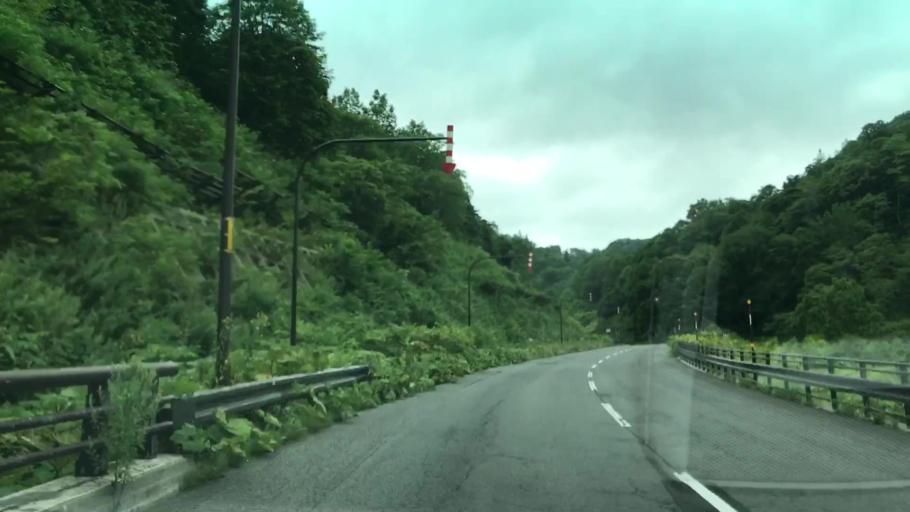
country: JP
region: Hokkaido
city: Yoichi
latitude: 42.9845
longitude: 140.8726
